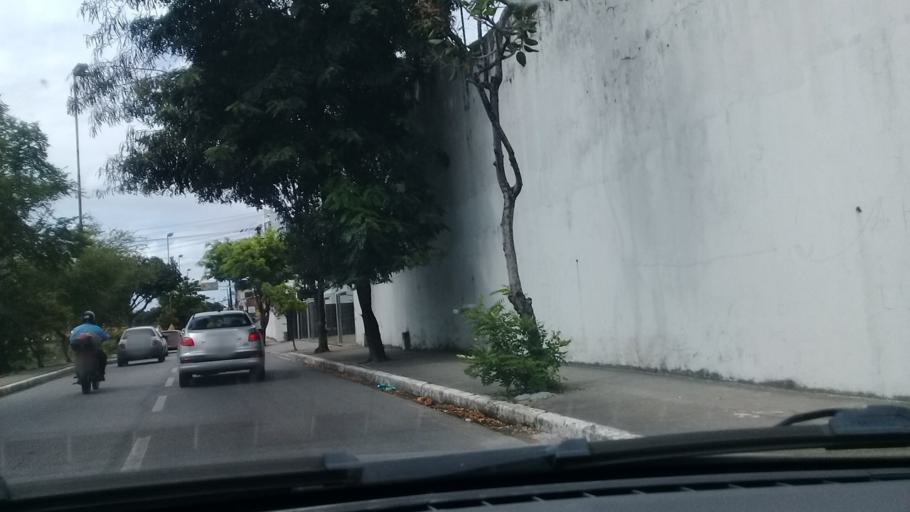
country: BR
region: Pernambuco
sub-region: Recife
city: Recife
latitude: -8.1307
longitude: -34.9105
